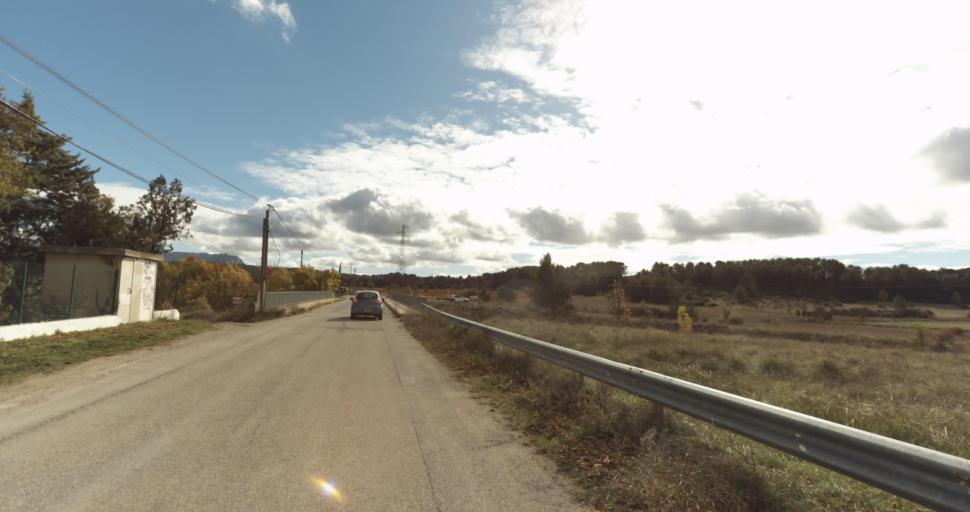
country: FR
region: Provence-Alpes-Cote d'Azur
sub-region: Departement des Bouches-du-Rhone
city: Venelles
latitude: 43.5837
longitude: 5.4926
